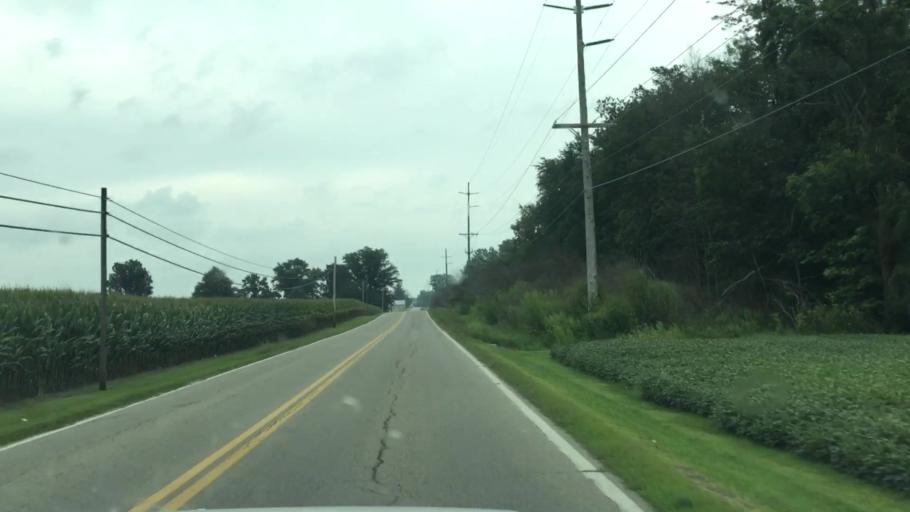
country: US
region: Ohio
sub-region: Clark County
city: Northridge
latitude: 39.9387
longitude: -83.7187
